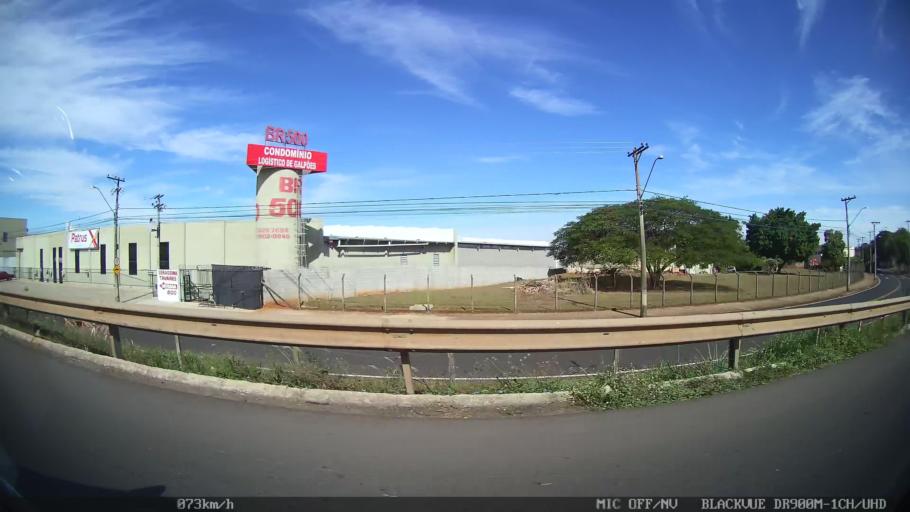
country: BR
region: Sao Paulo
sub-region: Sao Jose Do Rio Preto
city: Sao Jose do Rio Preto
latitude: -20.8028
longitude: -49.3543
